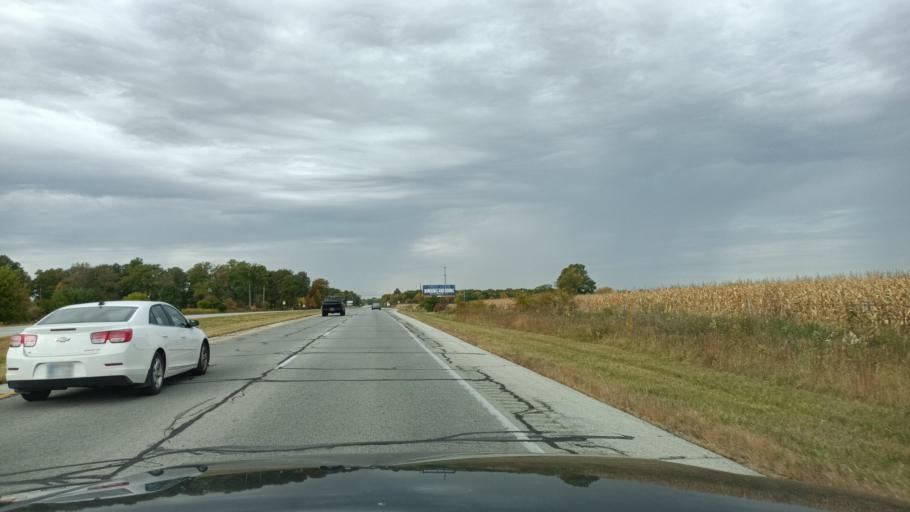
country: US
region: Indiana
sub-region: Delaware County
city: Yorktown
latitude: 40.2193
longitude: -85.4965
